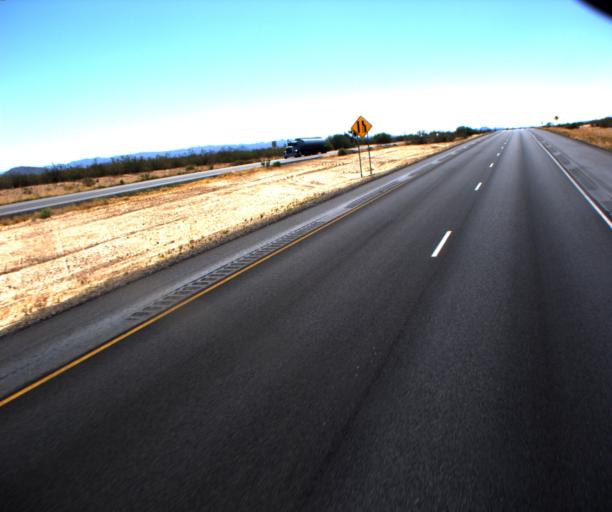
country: US
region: Arizona
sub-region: Yavapai County
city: Congress
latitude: 34.0587
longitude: -112.8582
